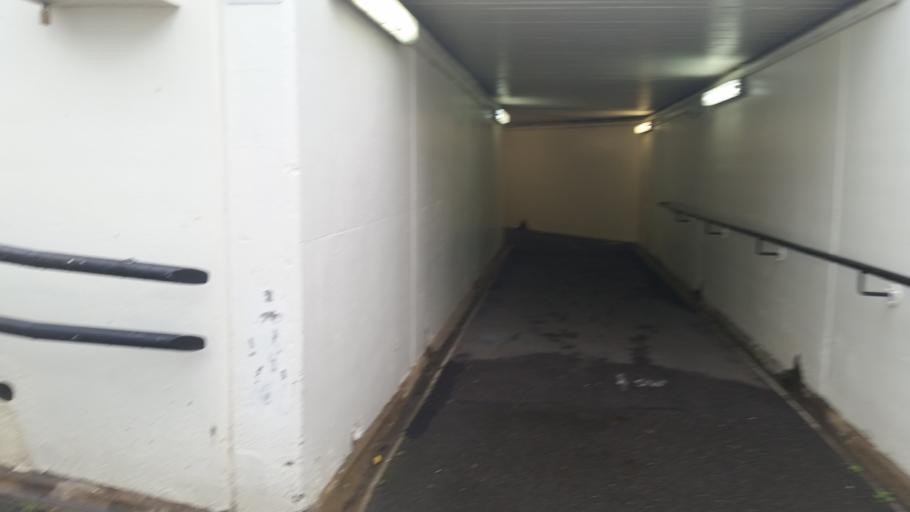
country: AU
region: Victoria
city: Albert Park
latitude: -37.8276
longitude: 145.0072
